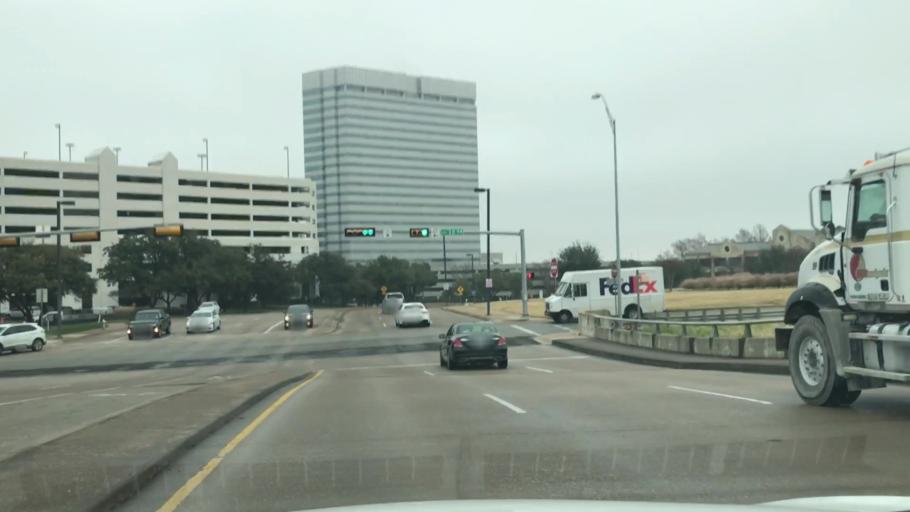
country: US
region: Texas
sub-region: Dallas County
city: Irving
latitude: 32.8582
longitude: -96.9326
